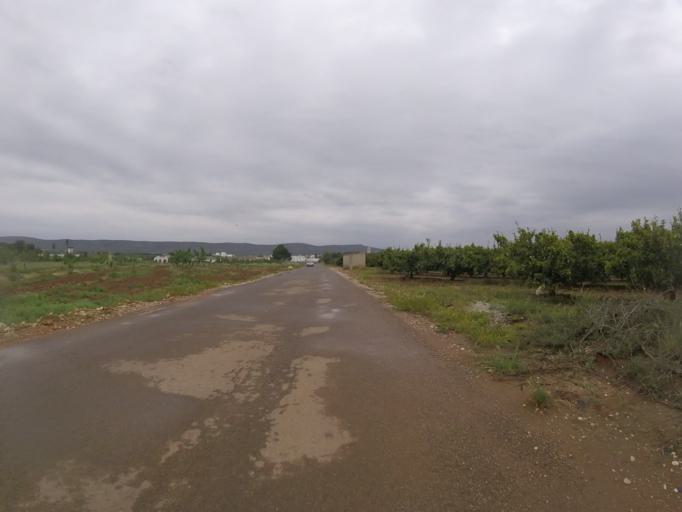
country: ES
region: Valencia
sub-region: Provincia de Castello
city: Alcala de Xivert
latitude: 40.2942
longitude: 0.2290
